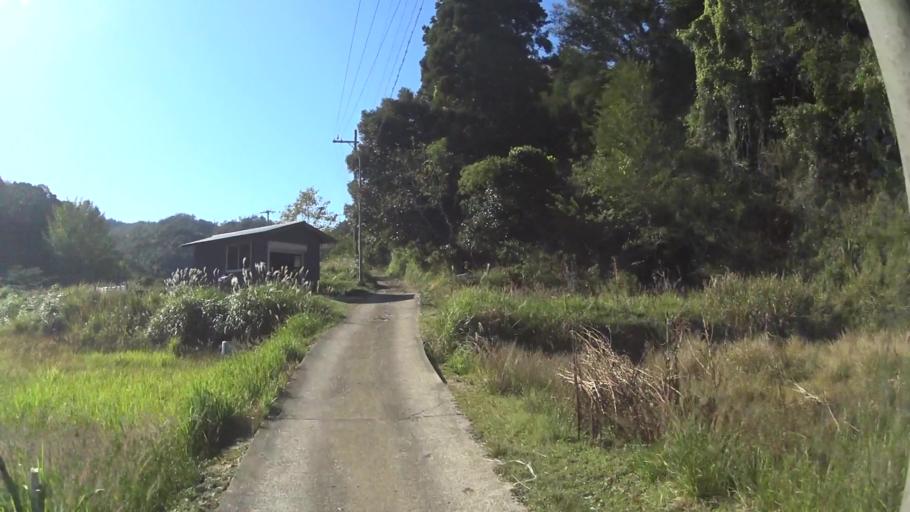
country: JP
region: Hyogo
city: Toyooka
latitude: 35.6479
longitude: 134.8790
